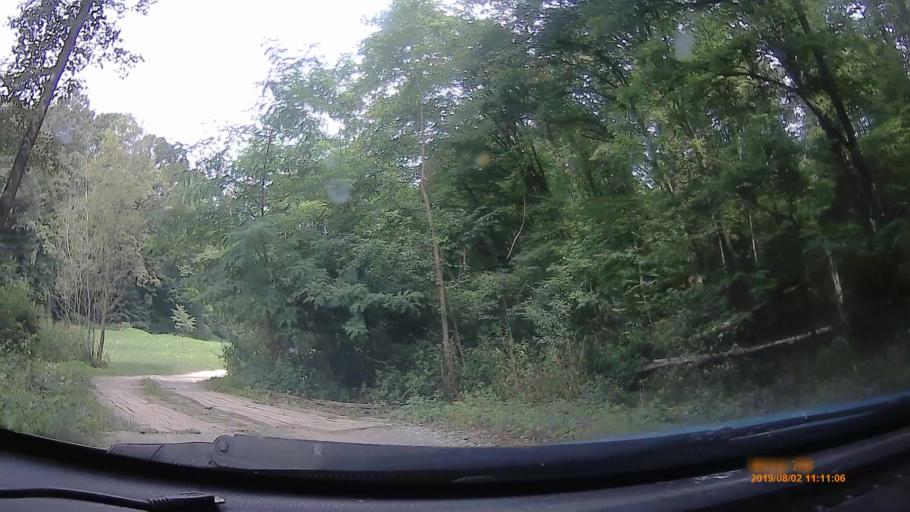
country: HU
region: Baranya
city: Buekkoesd
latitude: 46.1062
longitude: 17.9364
